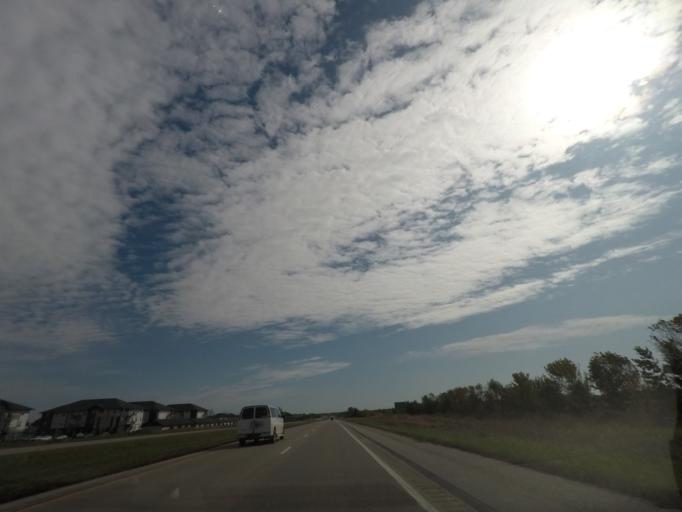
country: US
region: Iowa
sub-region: Story County
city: Ames
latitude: 42.0136
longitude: -93.6963
